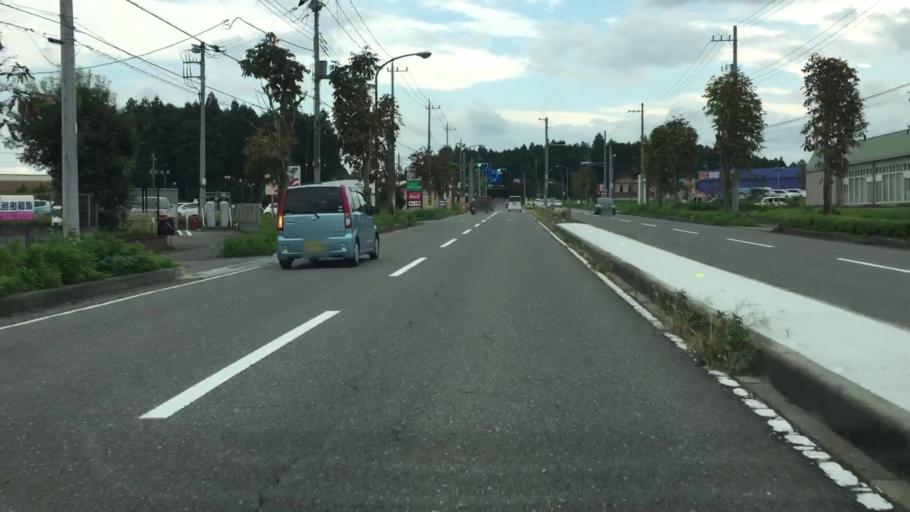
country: JP
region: Tochigi
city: Imaichi
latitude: 36.7443
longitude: 139.7127
